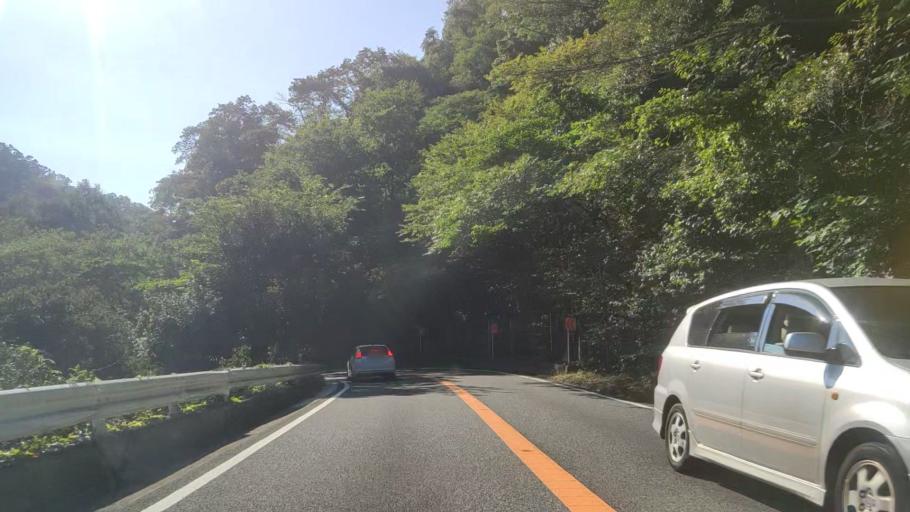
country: JP
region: Hyogo
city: Kobe
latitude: 34.6964
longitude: 135.1650
